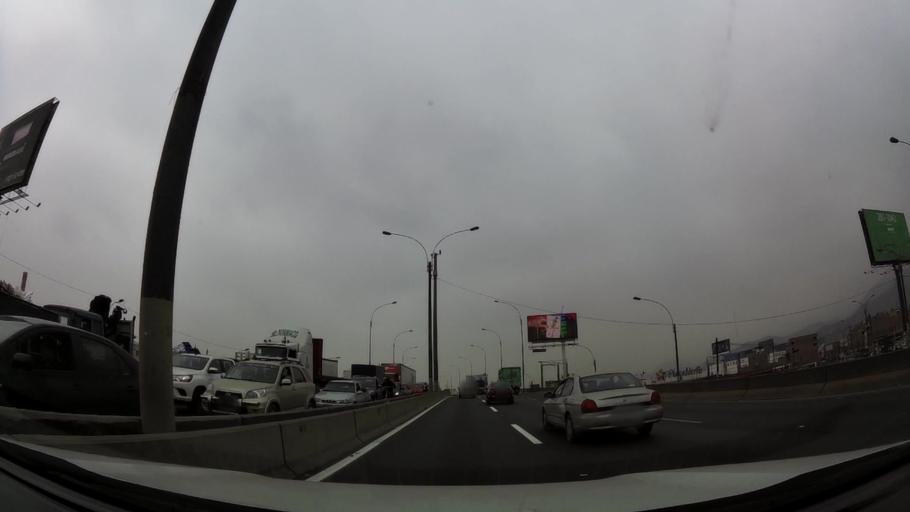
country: PE
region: Lima
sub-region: Lima
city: Independencia
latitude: -12.0104
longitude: -77.0608
